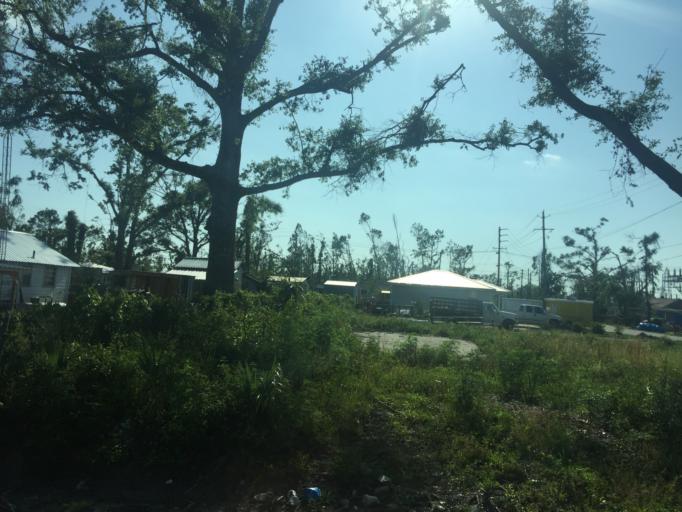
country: US
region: Florida
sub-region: Bay County
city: Cedar Grove
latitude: 30.1583
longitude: -85.6356
